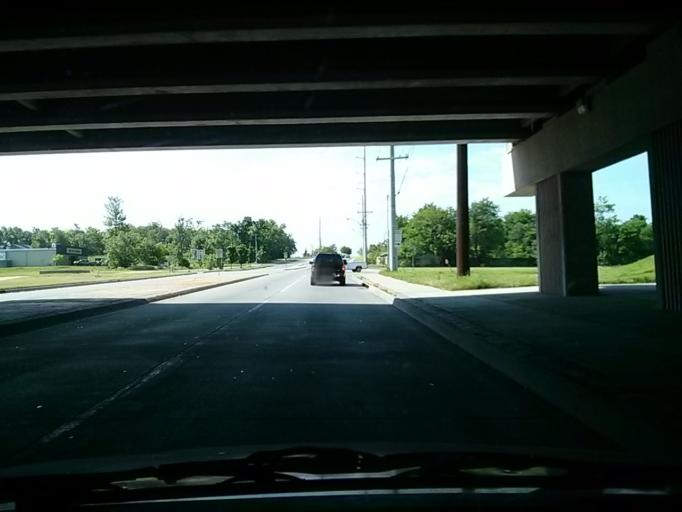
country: US
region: Oklahoma
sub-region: Tulsa County
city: Turley
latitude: 36.1974
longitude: -95.9757
